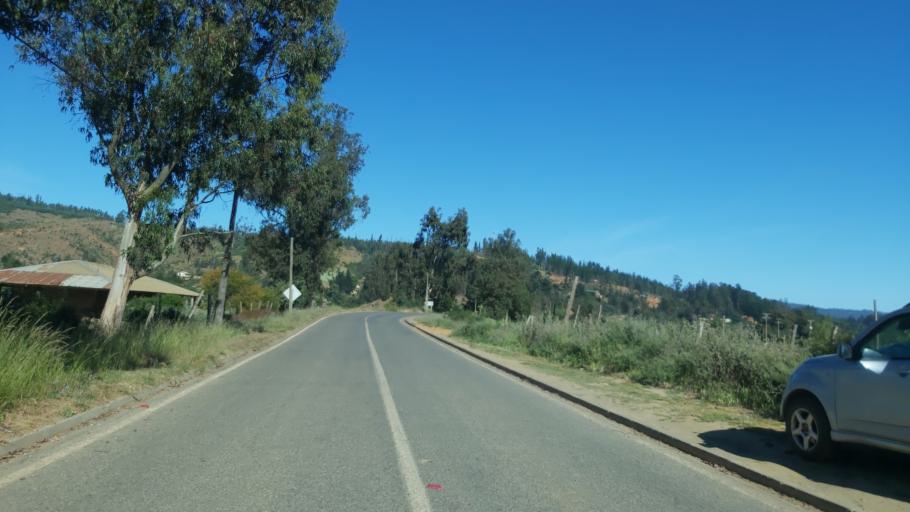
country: CL
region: Maule
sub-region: Provincia de Talca
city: Constitucion
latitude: -34.8515
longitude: -72.0408
